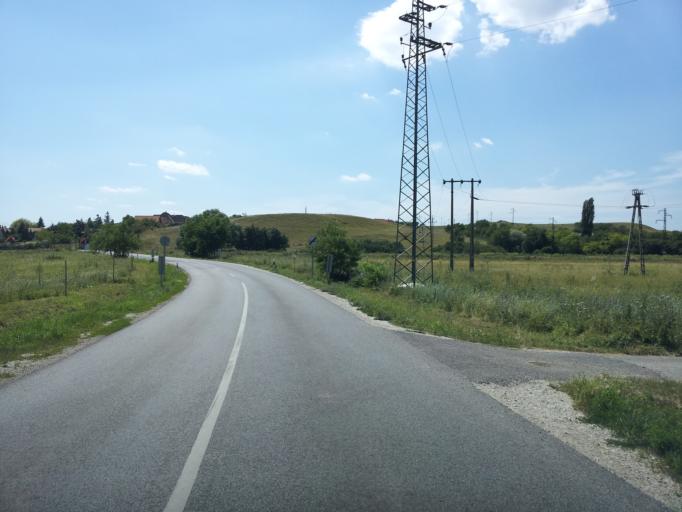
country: HU
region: Veszprem
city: Hajmasker
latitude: 47.1121
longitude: 18.0534
